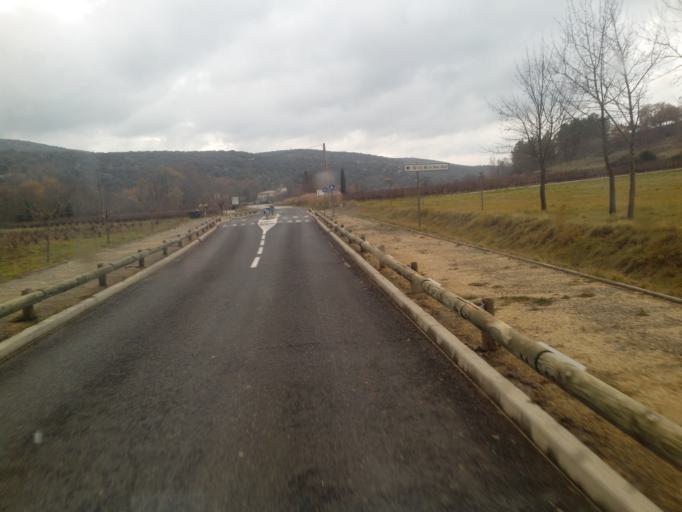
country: FR
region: Languedoc-Roussillon
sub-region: Departement de l'Herault
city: Saint-Bauzille-de-Putois
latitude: 43.9270
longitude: 3.7936
